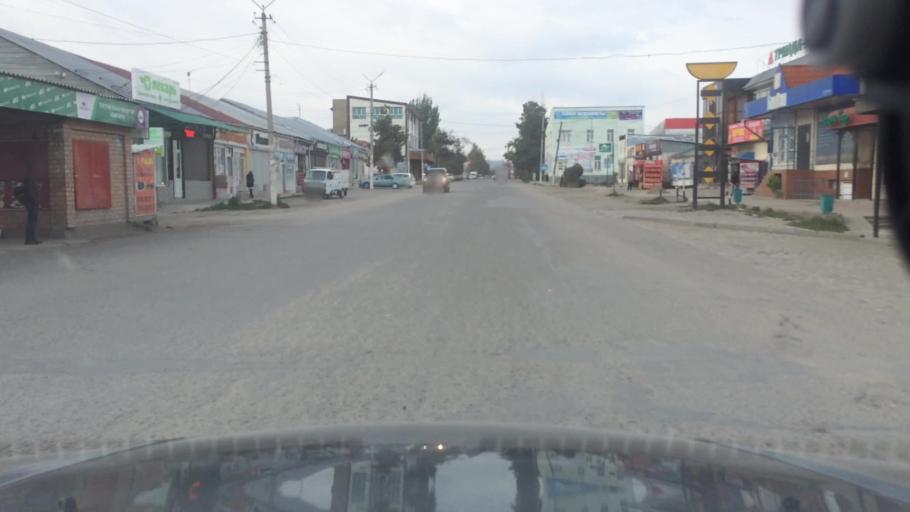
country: KG
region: Ysyk-Koel
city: Karakol
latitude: 42.4911
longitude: 78.3931
